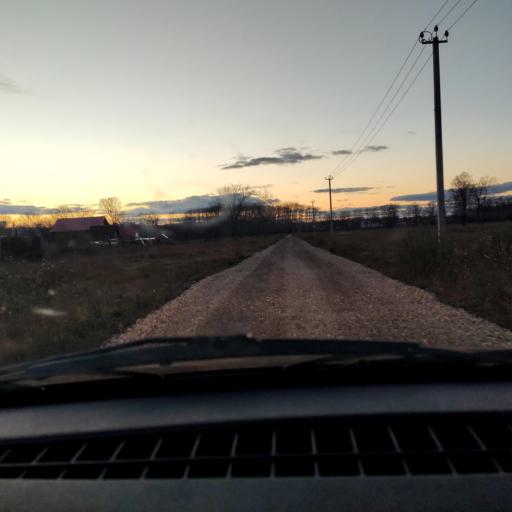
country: RU
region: Bashkortostan
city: Ufa
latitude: 54.6465
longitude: 55.9057
